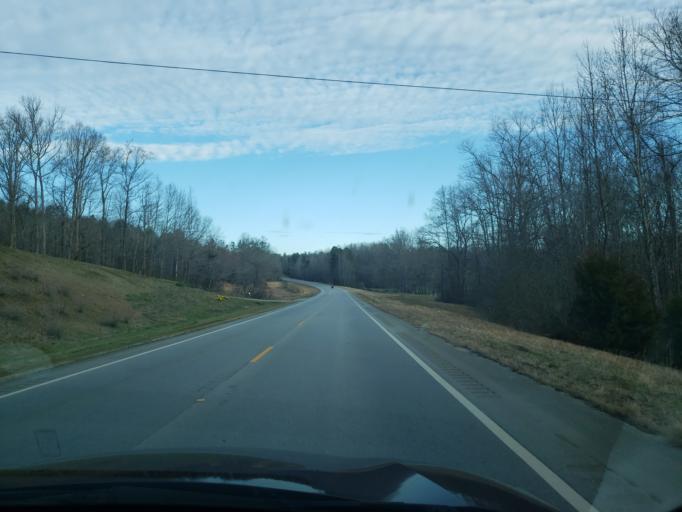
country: US
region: Alabama
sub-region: Randolph County
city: Wedowee
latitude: 33.3992
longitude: -85.5278
